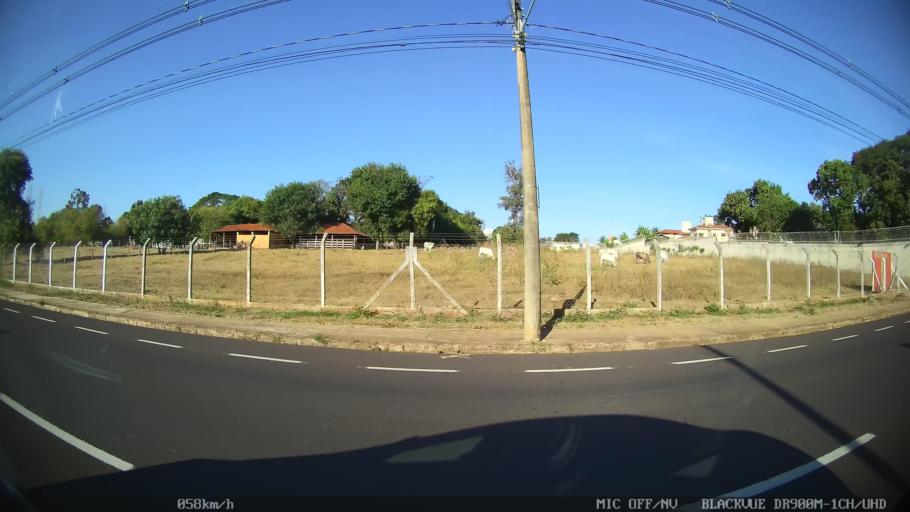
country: BR
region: Sao Paulo
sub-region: Sao Jose Do Rio Preto
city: Sao Jose do Rio Preto
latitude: -20.8451
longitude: -49.4115
